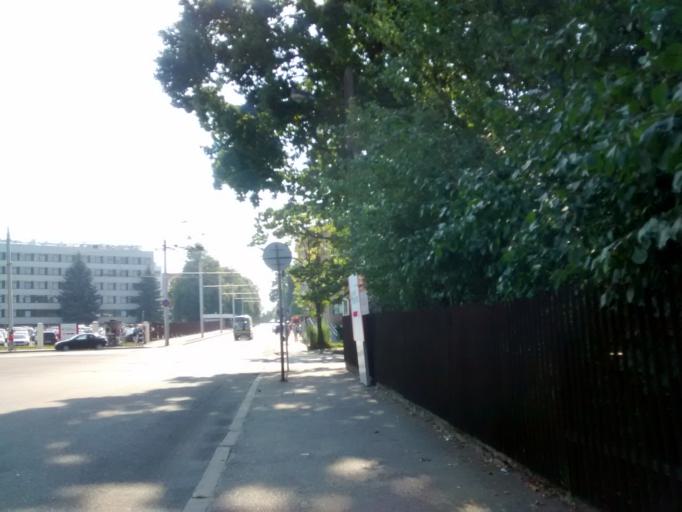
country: LT
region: Kauno apskritis
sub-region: Kaunas
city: Eiguliai
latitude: 54.9172
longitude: 23.9205
